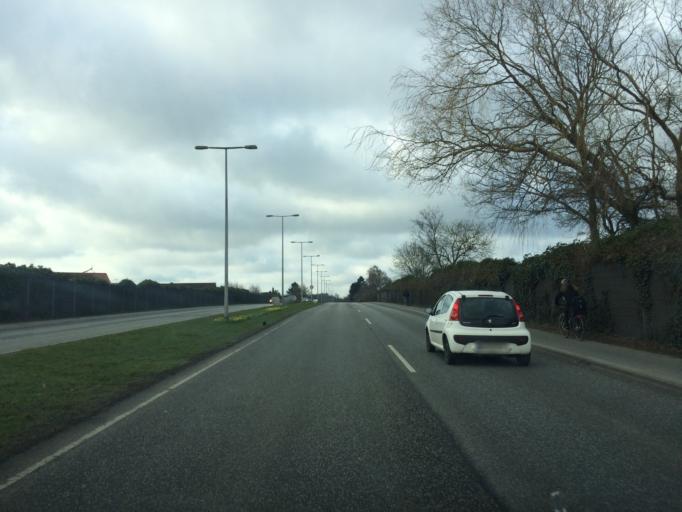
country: DK
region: South Denmark
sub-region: Fredericia Kommune
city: Snoghoj
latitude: 55.5478
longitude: 9.7232
